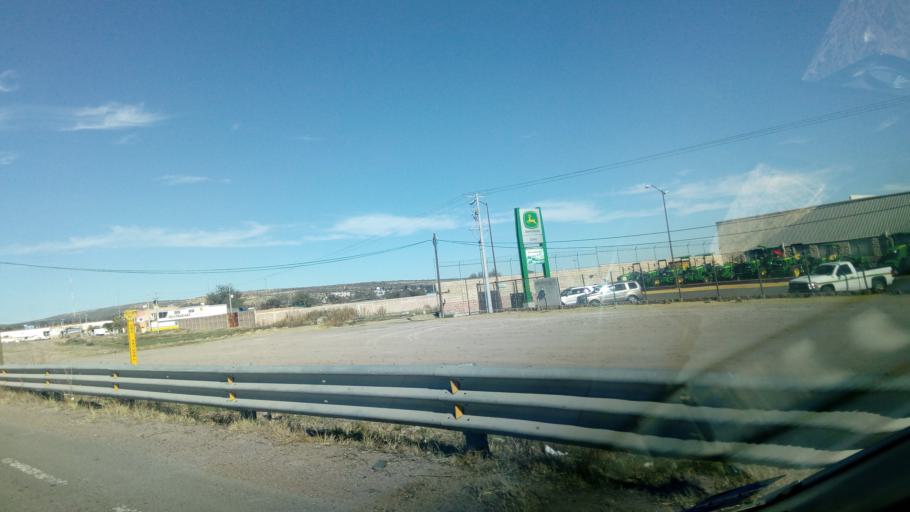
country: MX
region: Durango
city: Victoria de Durango
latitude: 24.0910
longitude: -104.5697
